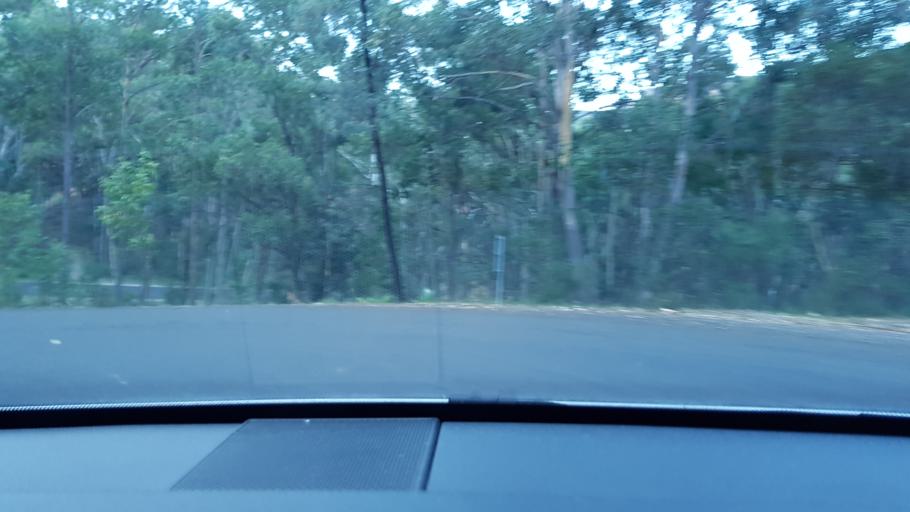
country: AU
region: New South Wales
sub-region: Lithgow
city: Portland
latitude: -33.3054
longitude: 150.1169
